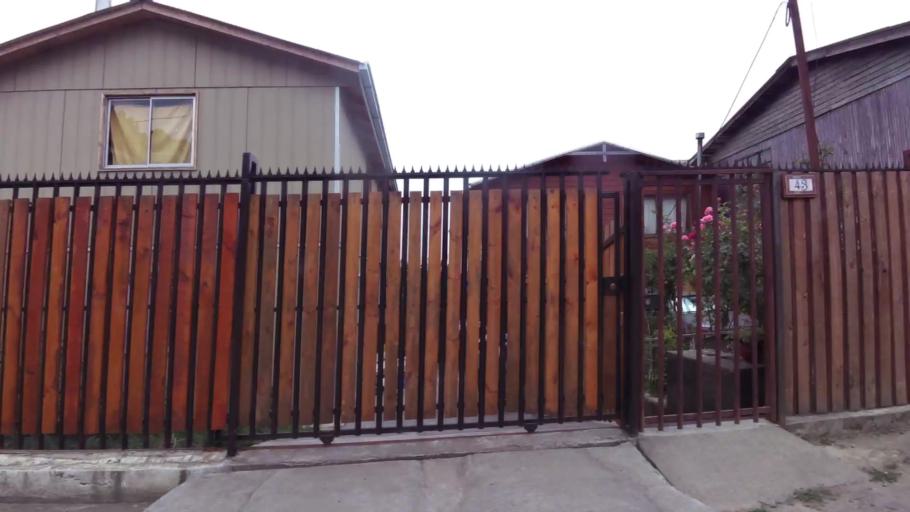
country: CL
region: Biobio
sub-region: Provincia de Concepcion
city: Concepcion
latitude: -36.8360
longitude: -73.0001
